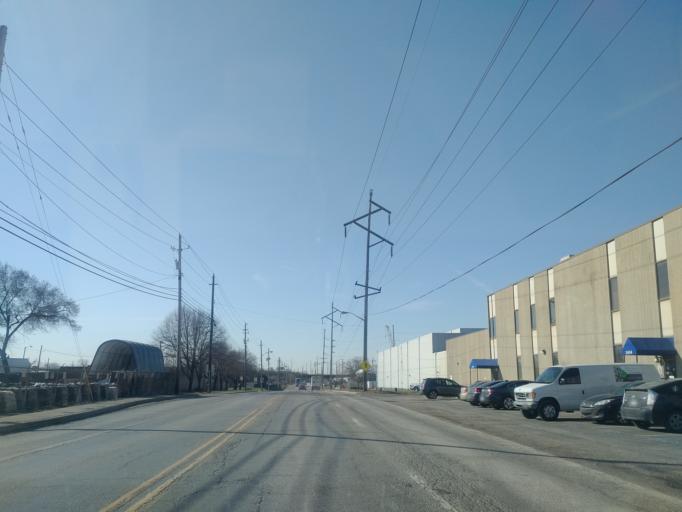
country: US
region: Indiana
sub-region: Marion County
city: Indianapolis
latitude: 39.7476
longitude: -86.1677
